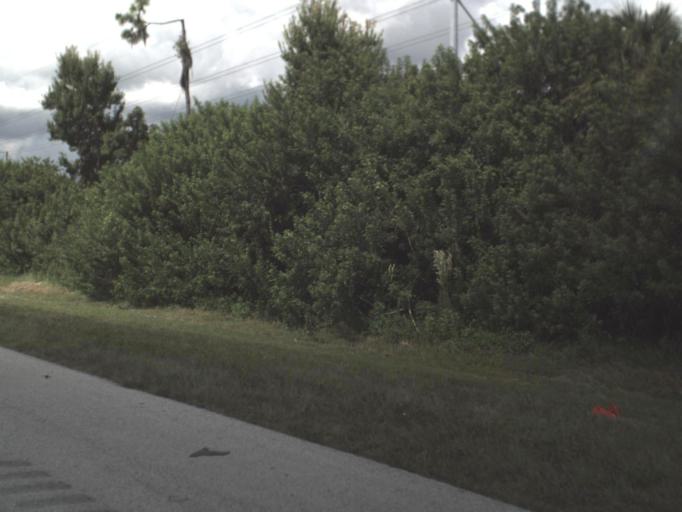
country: US
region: Florida
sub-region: Hillsborough County
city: Ruskin
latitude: 27.6818
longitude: -82.4239
